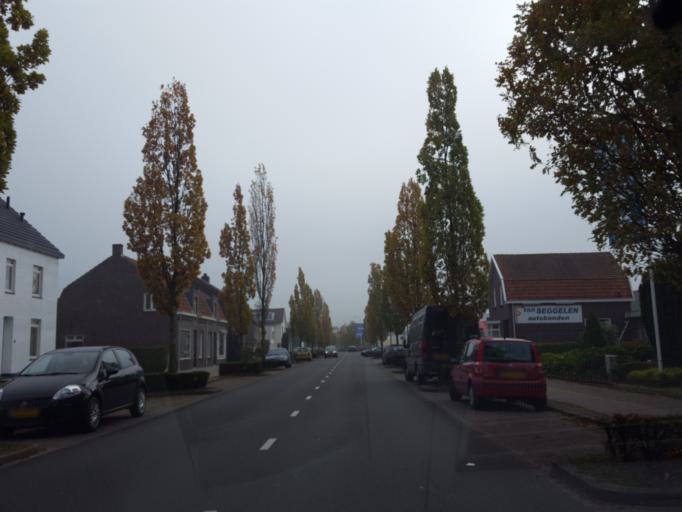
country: NL
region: Limburg
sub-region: Gemeente Weert
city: Weert
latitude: 51.2497
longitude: 5.7198
